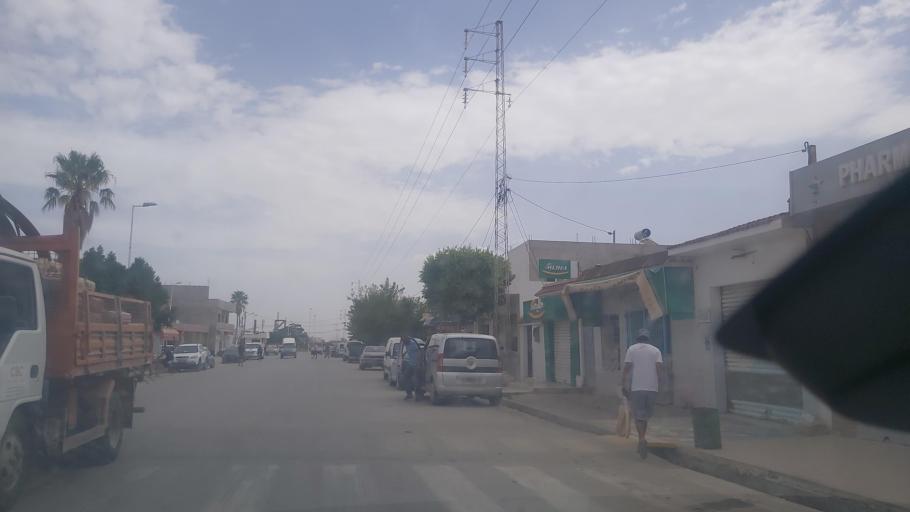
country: TN
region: Silyanah
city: Bu `Aradah
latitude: 36.3510
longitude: 9.6222
